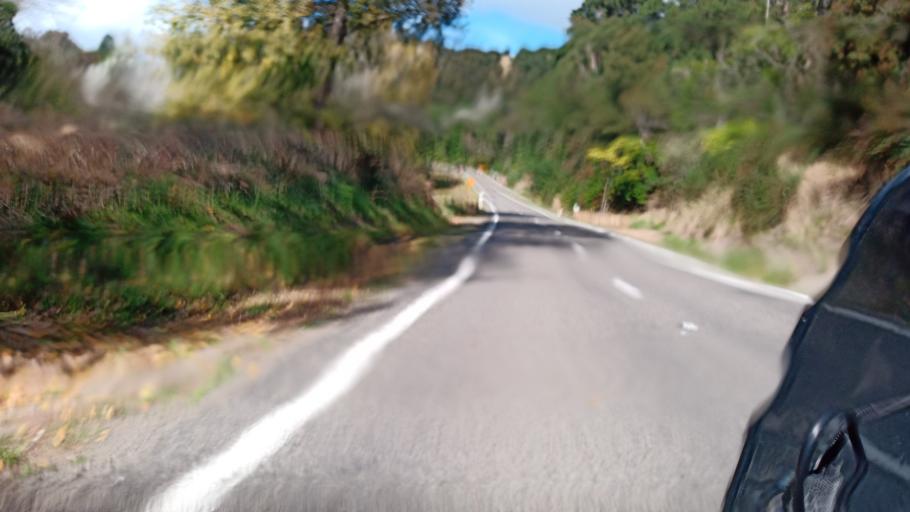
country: NZ
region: Gisborne
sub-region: Gisborne District
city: Gisborne
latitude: -38.4705
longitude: 177.6661
